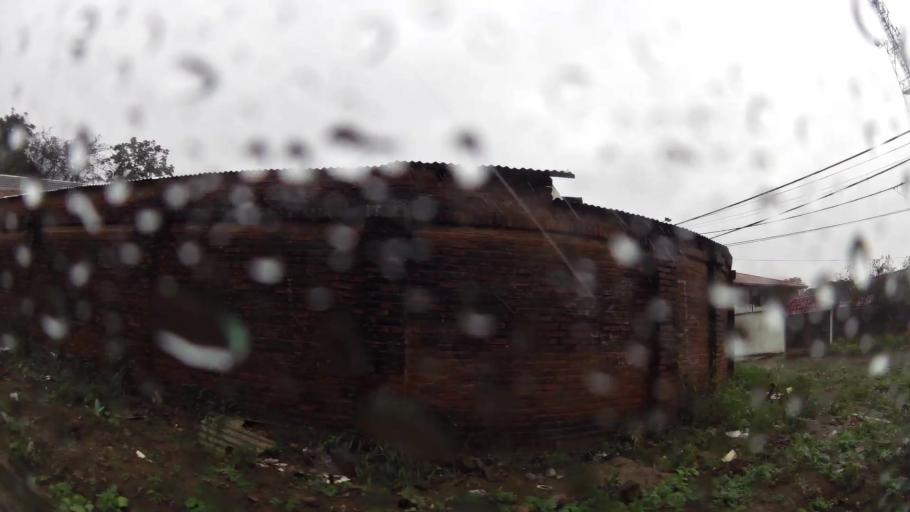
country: BO
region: Santa Cruz
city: Santa Cruz de la Sierra
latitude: -17.8056
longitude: -63.1619
